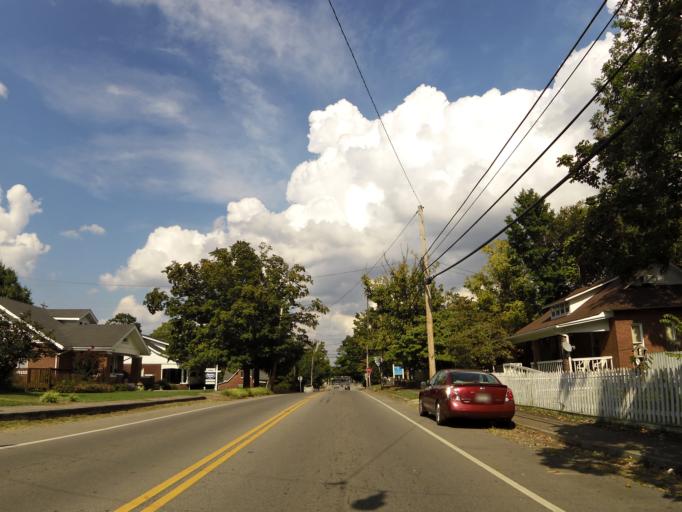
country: US
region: Tennessee
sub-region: Dickson County
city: Dickson
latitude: 36.0721
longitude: -87.3922
